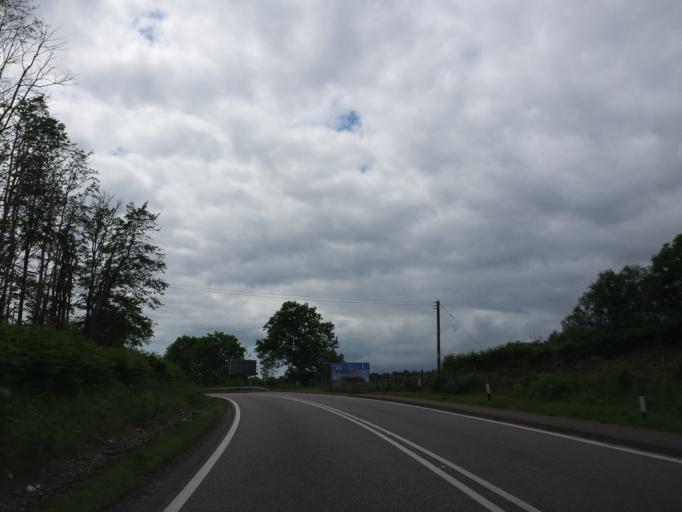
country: GB
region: Scotland
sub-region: Argyll and Bute
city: Oban
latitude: 56.4304
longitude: -5.4586
